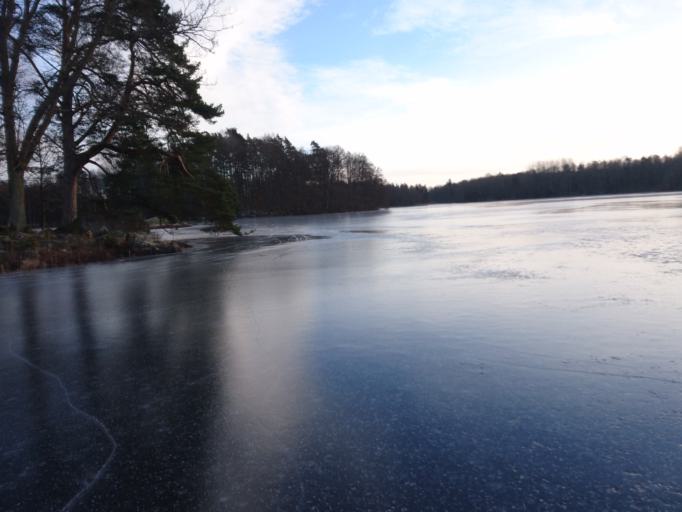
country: SE
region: Blekinge
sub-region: Karlshamns Kommun
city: Karlshamn
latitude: 56.2385
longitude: 14.9670
